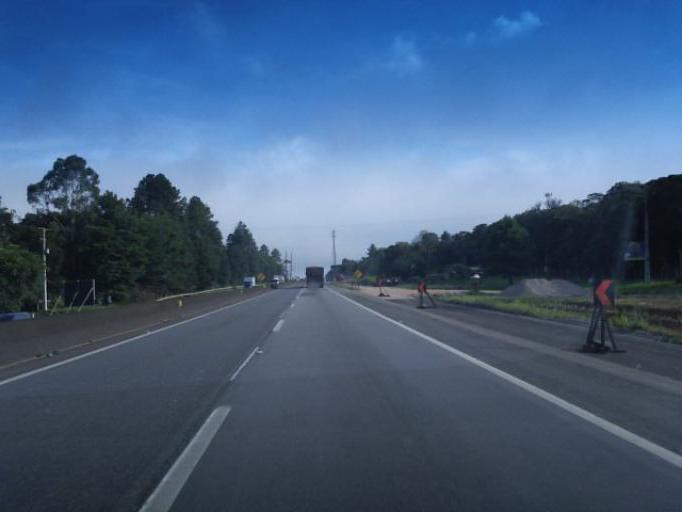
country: BR
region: Parana
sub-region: Sao Jose Dos Pinhais
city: Sao Jose dos Pinhais
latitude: -25.7733
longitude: -49.1215
